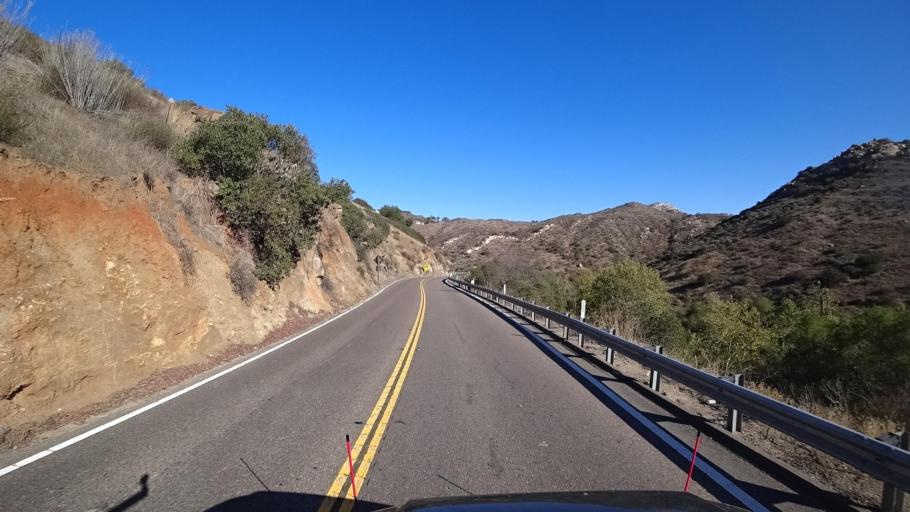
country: US
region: California
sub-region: San Diego County
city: Jamul
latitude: 32.6510
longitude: -116.7885
